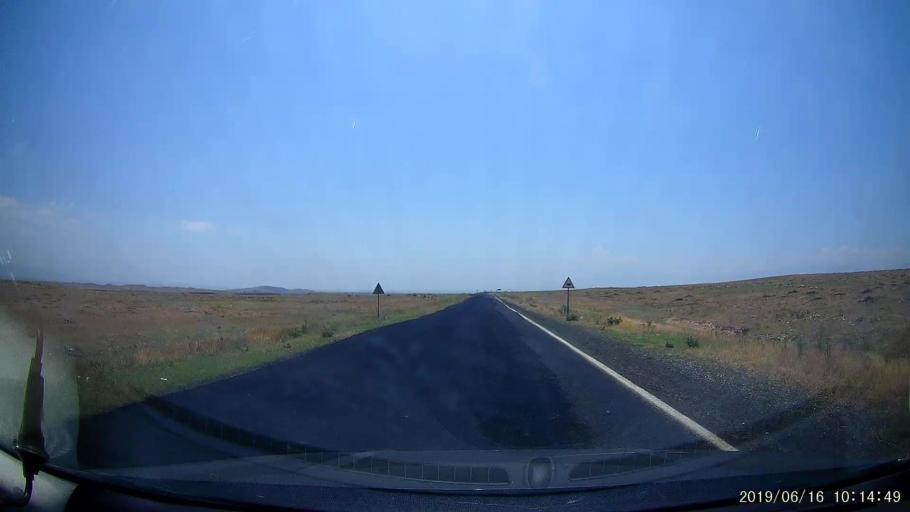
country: TR
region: Igdir
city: Tuzluca
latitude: 40.1814
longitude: 43.6707
